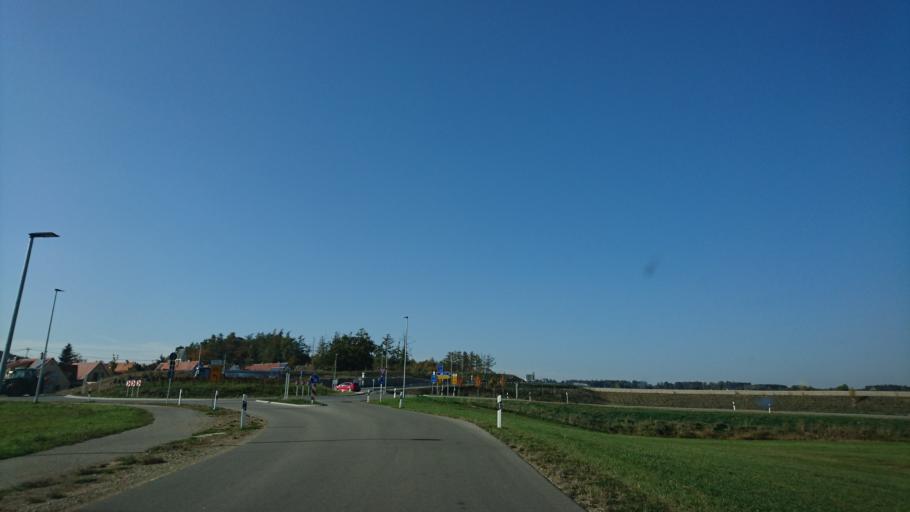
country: DE
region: Bavaria
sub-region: Swabia
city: Zusmarshausen
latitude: 48.4074
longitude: 10.5894
